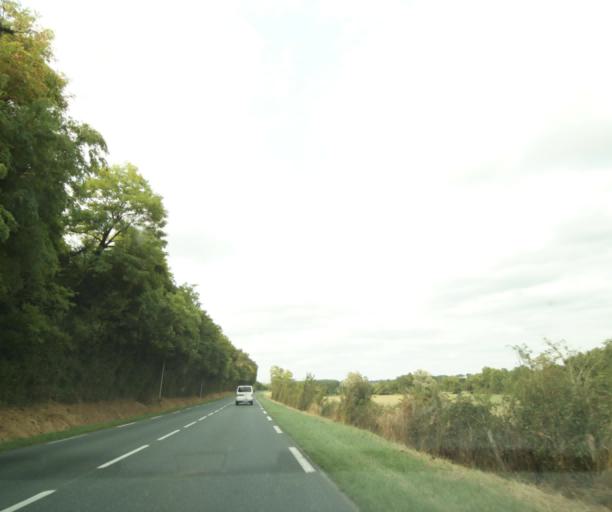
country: FR
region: Centre
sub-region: Departement de l'Indre
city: Clion
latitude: 46.9510
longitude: 1.2150
